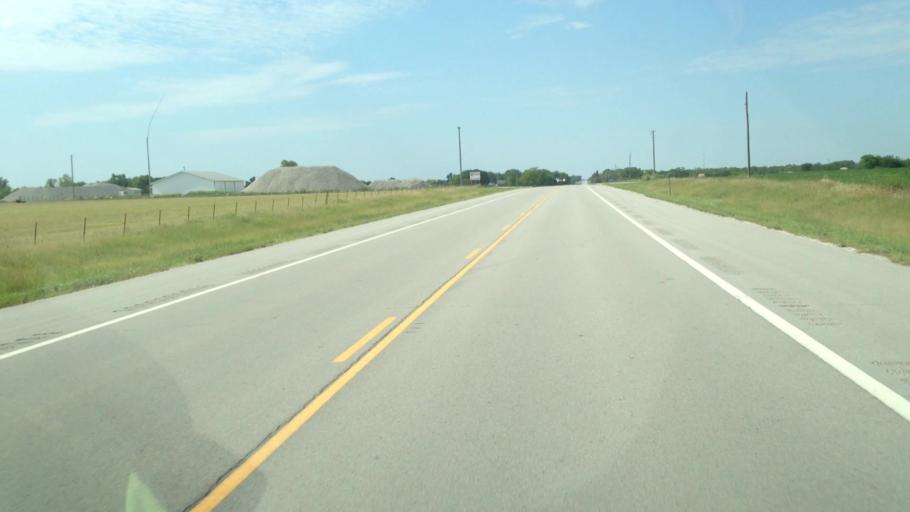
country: US
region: Kansas
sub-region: Labette County
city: Parsons
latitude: 37.2796
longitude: -95.2675
